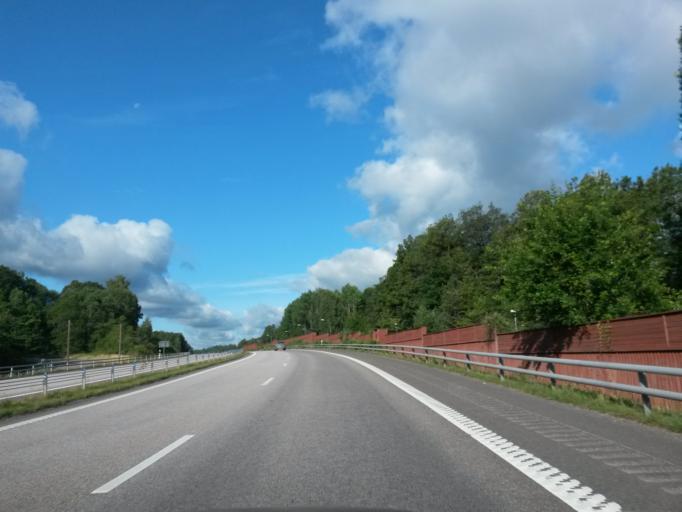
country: SE
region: Vaestra Goetaland
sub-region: Lerums Kommun
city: Stenkullen
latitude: 57.8076
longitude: 12.3822
